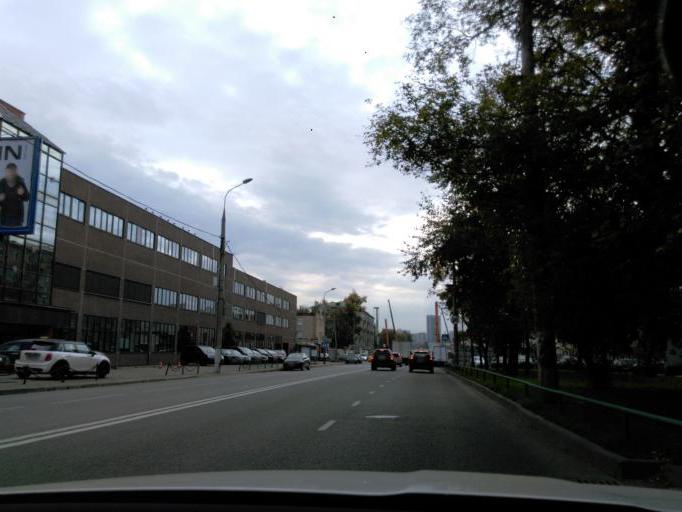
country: RU
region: Moscow
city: Ostankinskiy
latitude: 55.8158
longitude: 37.5990
